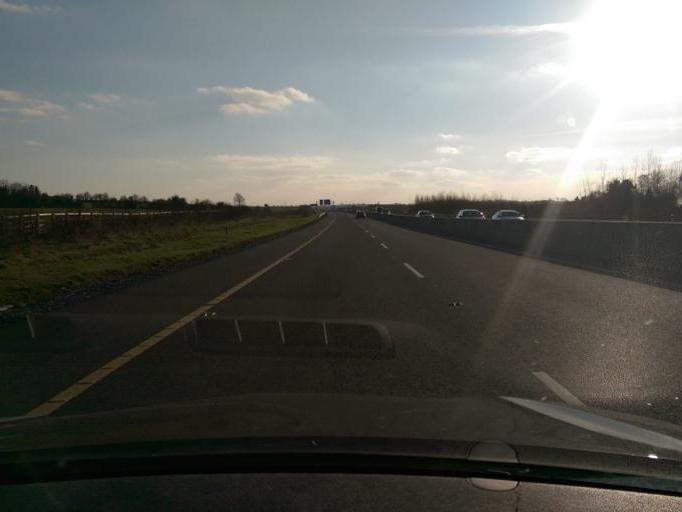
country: IE
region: Leinster
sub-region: Laois
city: Mountrath
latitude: 52.9375
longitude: -7.4590
